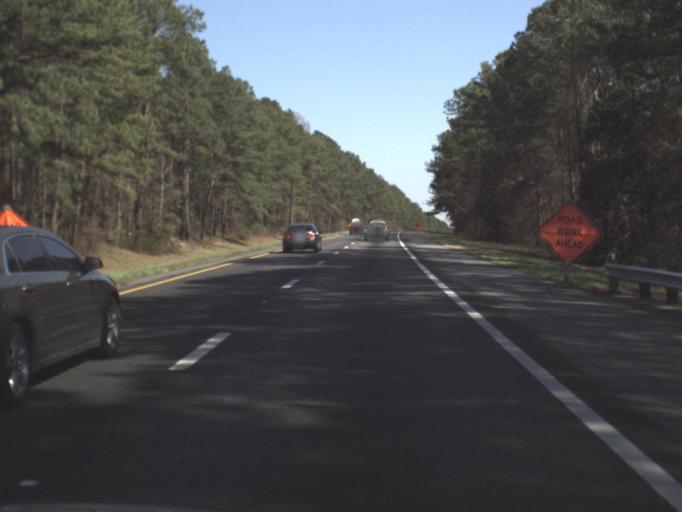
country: US
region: Florida
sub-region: Gadsden County
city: Chattahoochee
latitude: 30.6295
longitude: -84.8618
